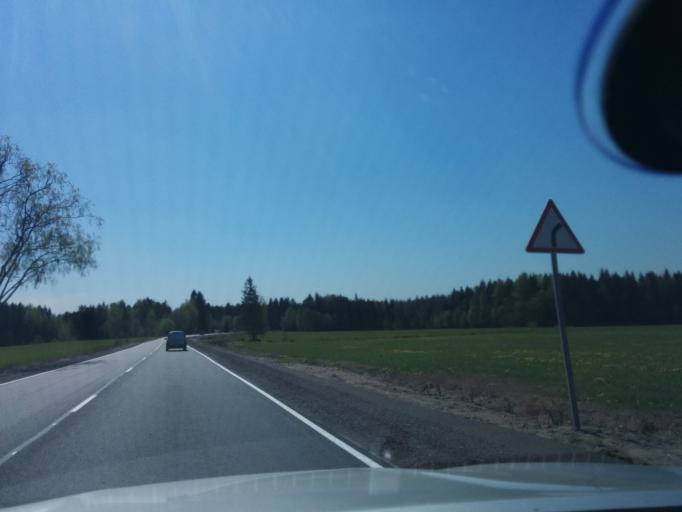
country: RU
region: Leningrad
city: Verkhniye Osel'ki
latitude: 60.2028
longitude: 30.4263
